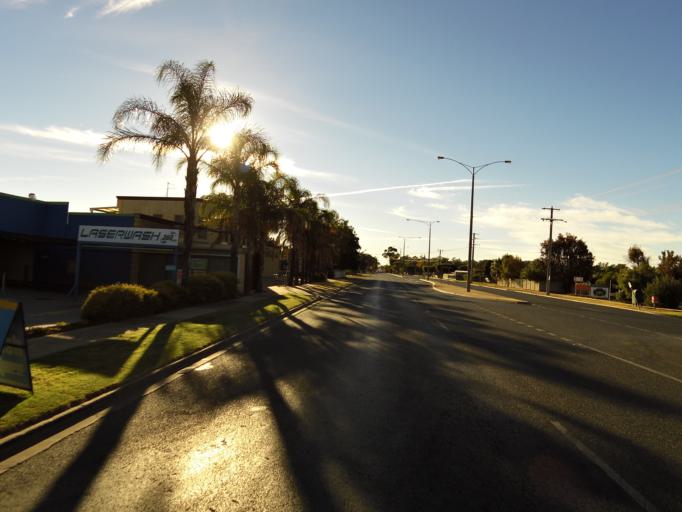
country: AU
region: Victoria
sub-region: Campaspe
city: Echuca
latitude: -36.1404
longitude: 144.7335
